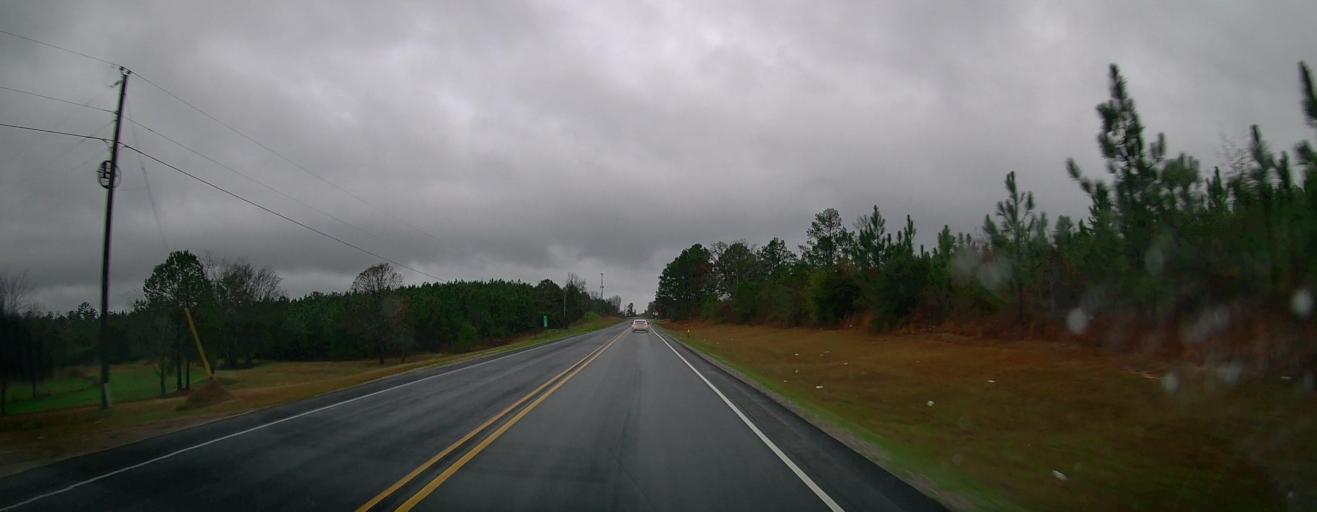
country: US
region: Alabama
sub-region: Chilton County
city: Clanton
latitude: 32.6331
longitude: -86.7475
